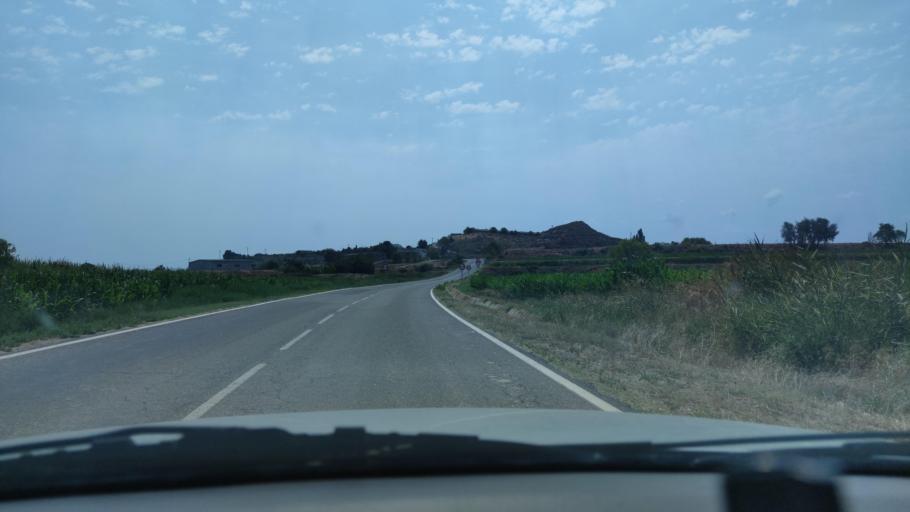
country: ES
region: Catalonia
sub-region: Provincia de Lleida
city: Bellpuig
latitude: 41.6137
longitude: 1.0278
